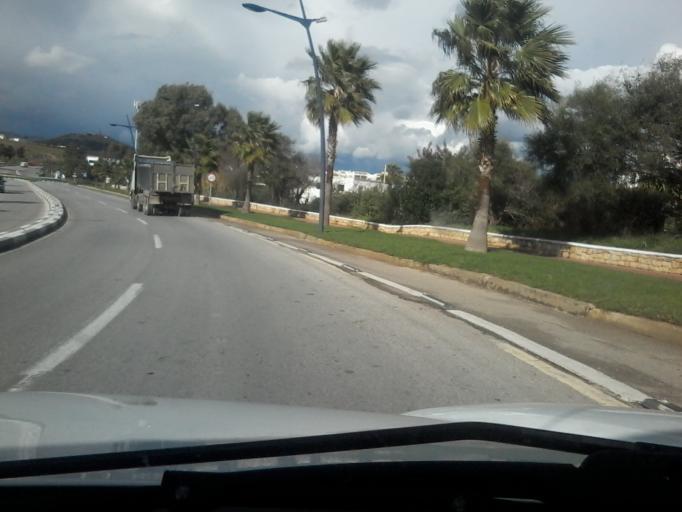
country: ES
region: Ceuta
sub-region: Ceuta
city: Ceuta
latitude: 35.7526
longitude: -5.3455
